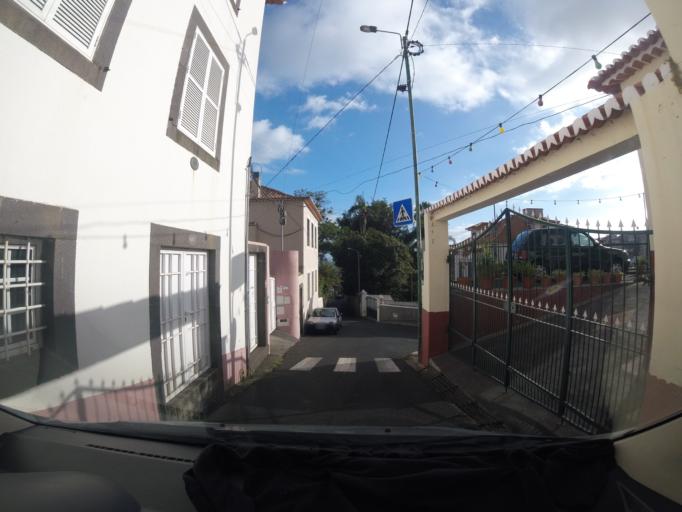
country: PT
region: Madeira
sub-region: Funchal
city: Nossa Senhora do Monte
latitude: 32.6566
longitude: -16.9108
